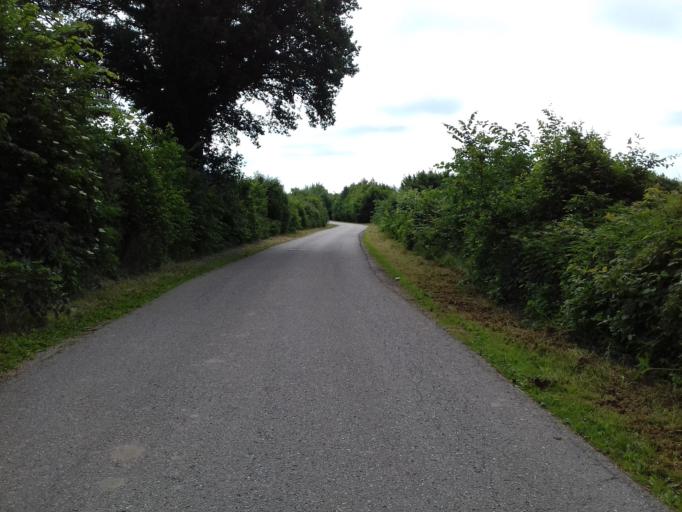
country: DE
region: Schleswig-Holstein
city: Tasdorf
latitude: 54.0769
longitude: 10.0172
